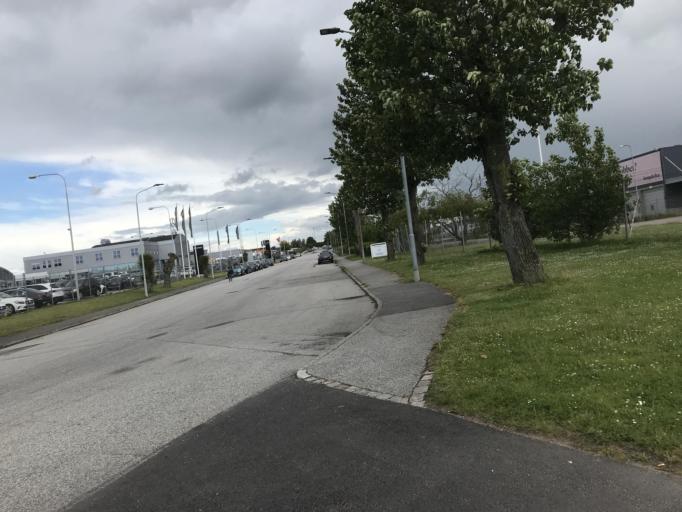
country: SE
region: Skane
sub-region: Malmo
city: Malmoe
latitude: 55.5649
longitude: 13.0398
